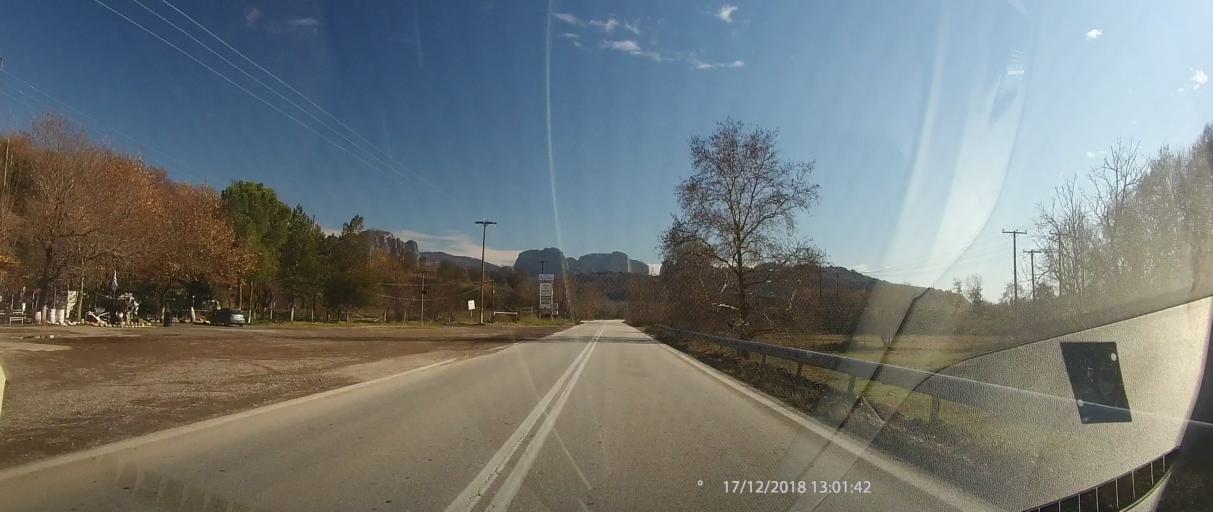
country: GR
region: Thessaly
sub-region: Trikala
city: Kastraki
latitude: 39.7309
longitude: 21.5869
